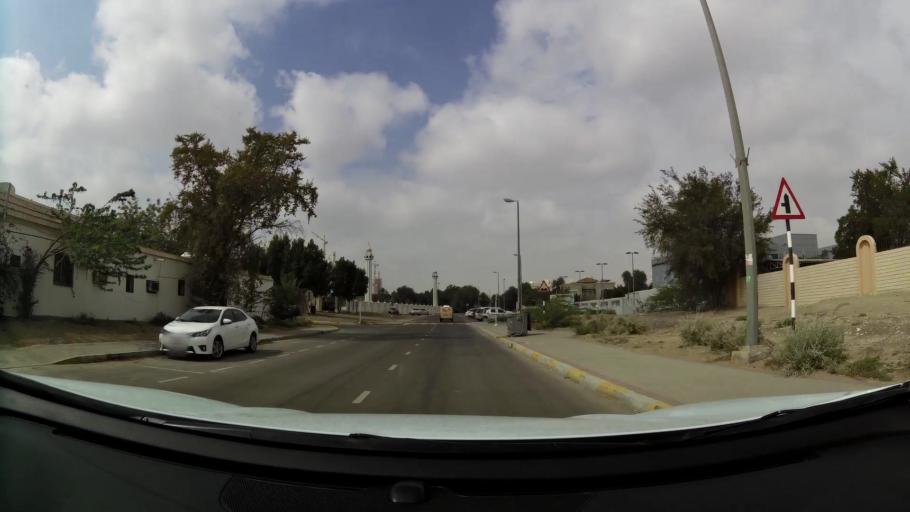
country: AE
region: Abu Dhabi
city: Al Ain
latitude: 24.2289
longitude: 55.7536
